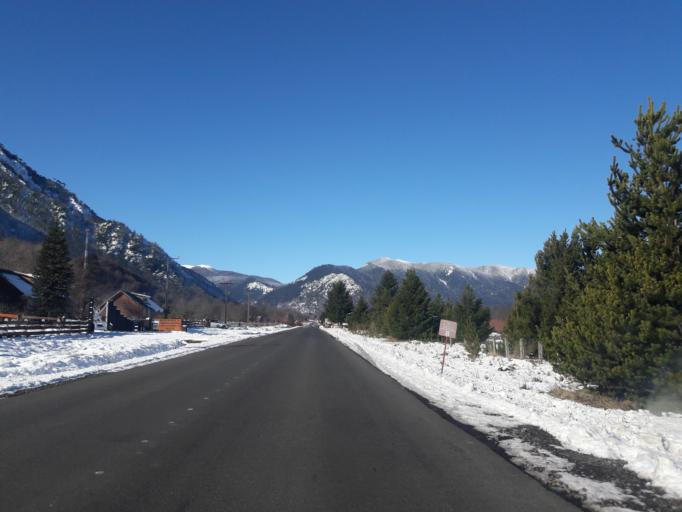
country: CL
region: Araucania
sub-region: Provincia de Cautin
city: Vilcun
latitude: -38.4716
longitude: -71.5715
